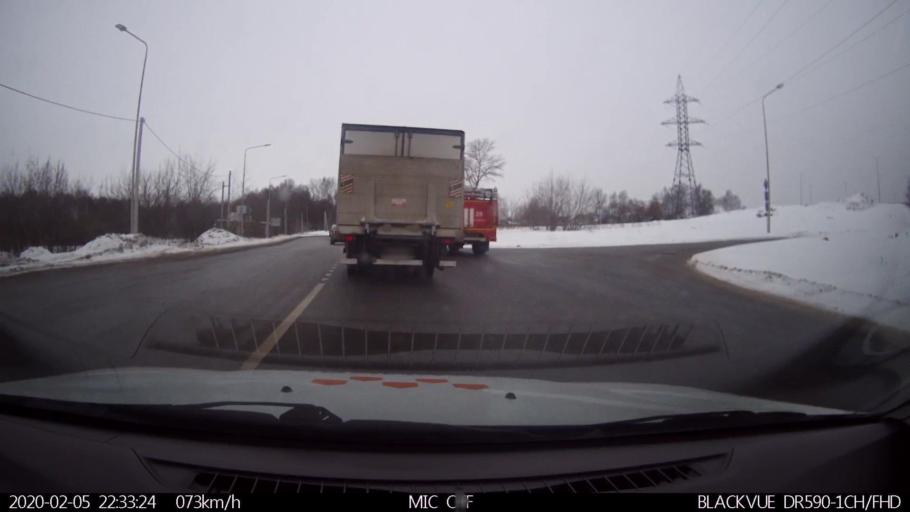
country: RU
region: Nizjnij Novgorod
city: Imeni Stepana Razina
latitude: 54.7365
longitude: 44.2096
